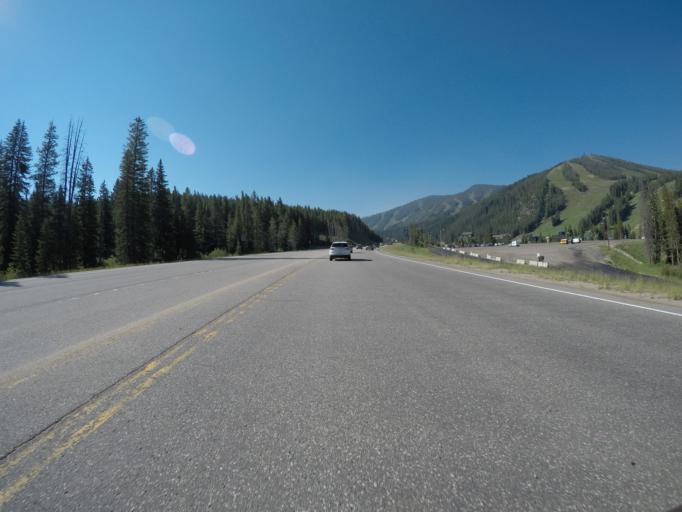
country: US
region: Colorado
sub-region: Grand County
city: Fraser
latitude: 39.8904
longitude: -105.7606
